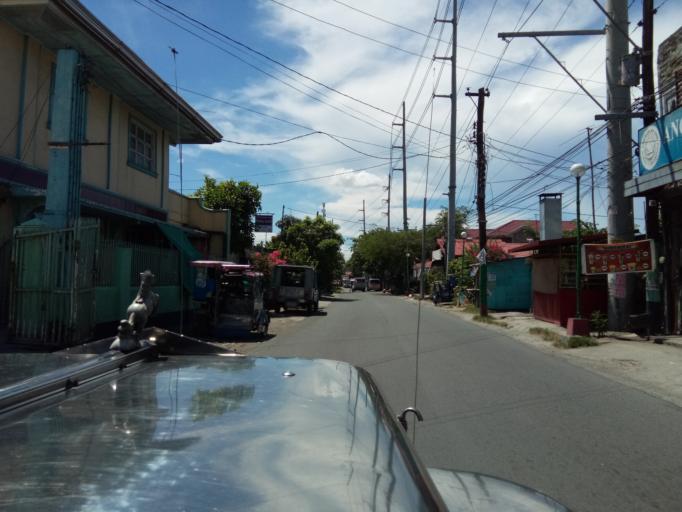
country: PH
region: Calabarzon
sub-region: Province of Cavite
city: Pasong Kawayan Primero
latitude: 14.3650
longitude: 120.8939
